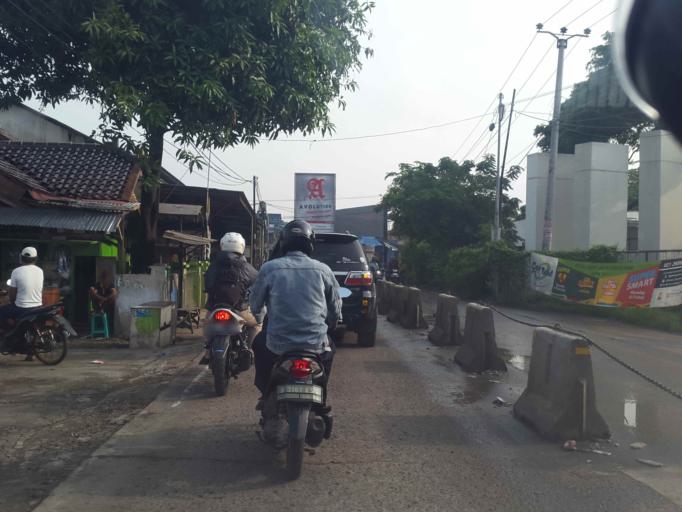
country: ID
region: West Java
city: Bekasi
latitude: -6.2763
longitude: 107.0418
